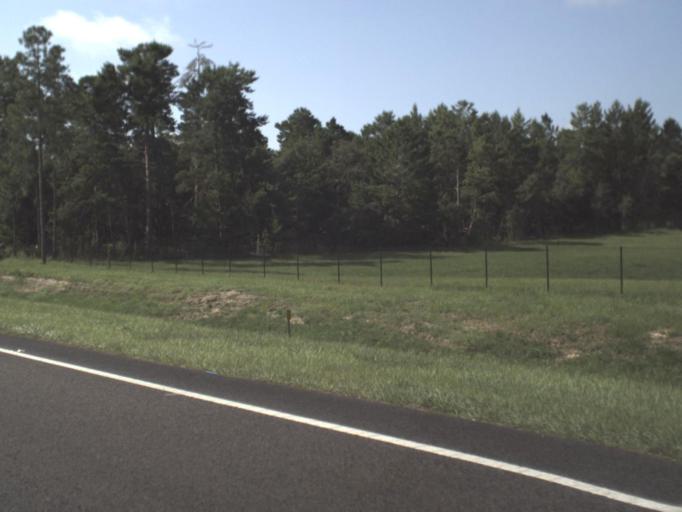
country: US
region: Florida
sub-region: Citrus County
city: Sugarmill Woods
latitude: 28.6821
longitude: -82.4915
